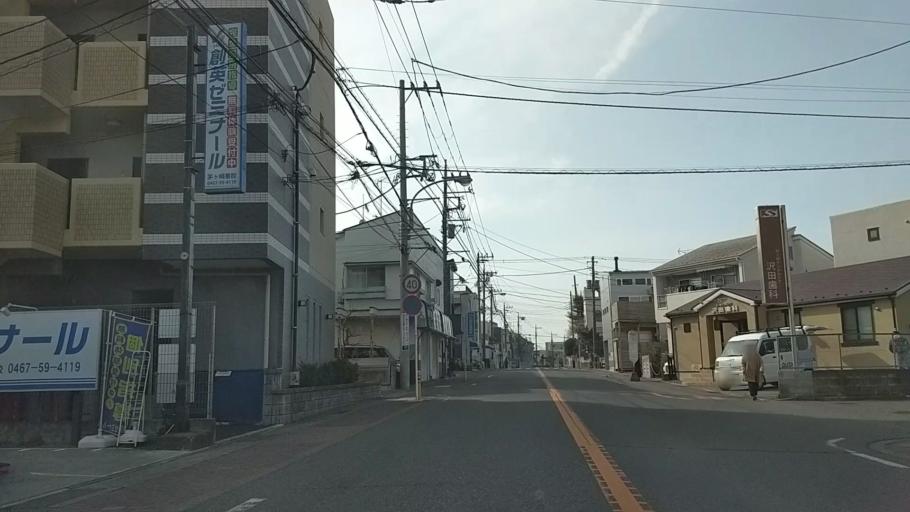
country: JP
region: Kanagawa
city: Chigasaki
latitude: 35.3327
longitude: 139.4299
